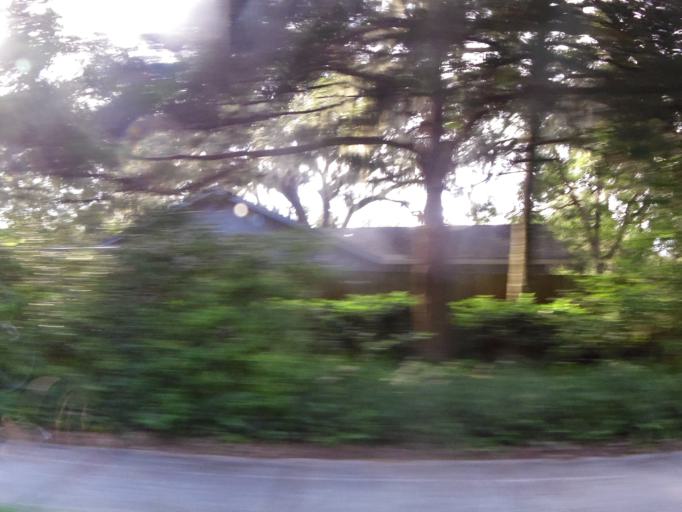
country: US
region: Florida
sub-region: Saint Johns County
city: Fruit Cove
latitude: 30.1574
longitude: -81.5990
